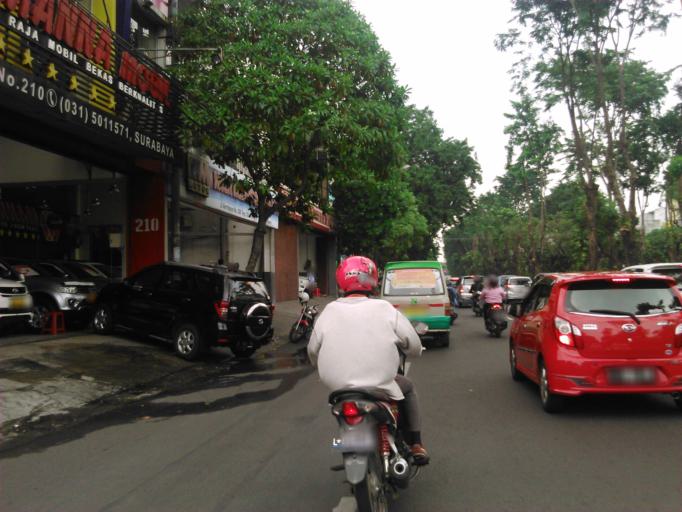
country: ID
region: East Java
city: Gubengairlangga
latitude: -7.2790
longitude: 112.7599
